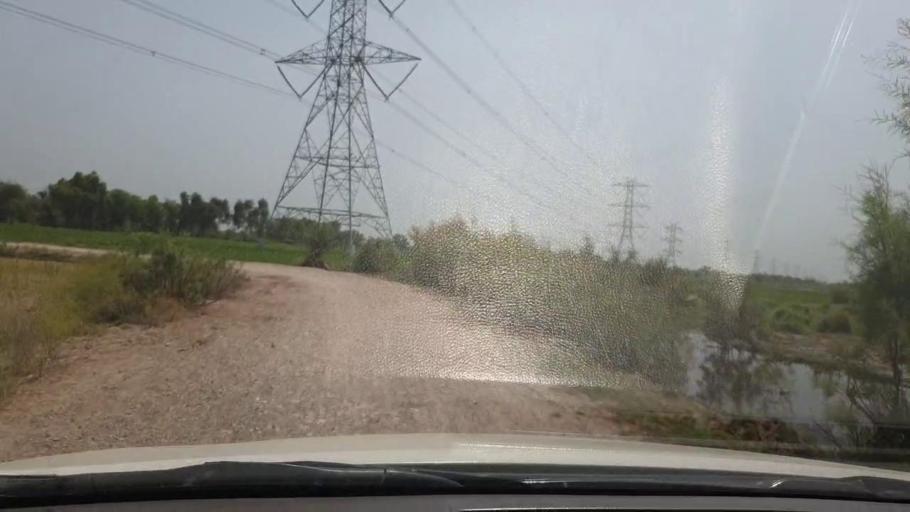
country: PK
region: Sindh
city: Shikarpur
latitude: 28.0281
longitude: 68.6479
